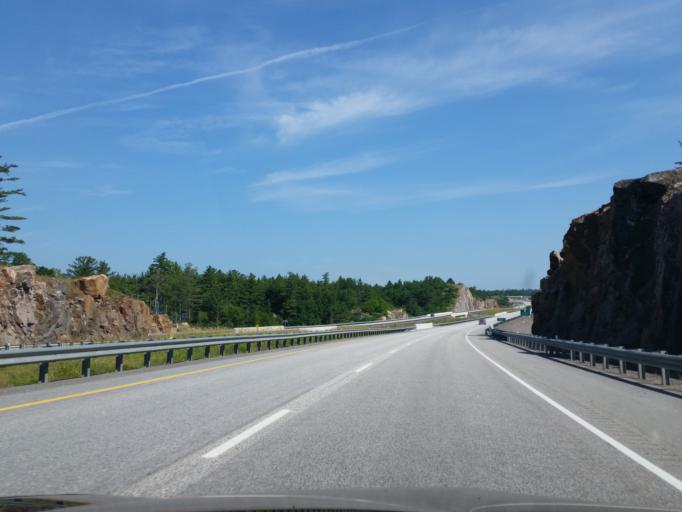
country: CA
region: Ontario
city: Greater Sudbury
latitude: 46.2119
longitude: -80.7688
